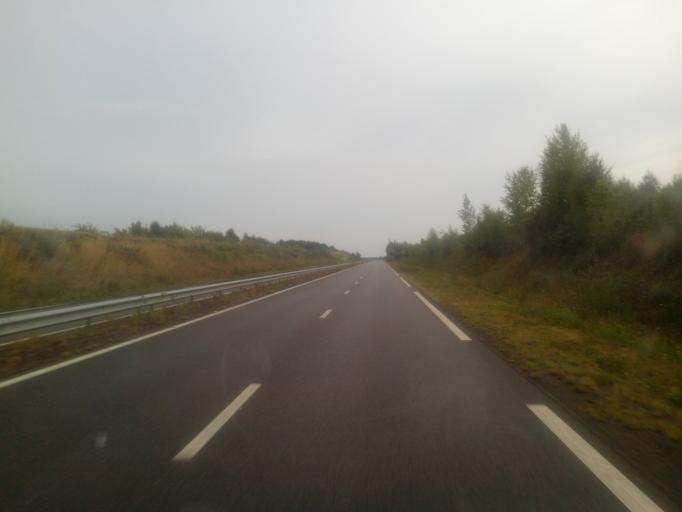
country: FR
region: Brittany
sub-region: Departement d'Ille-et-Vilaine
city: Betton
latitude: 48.1752
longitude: -1.6257
